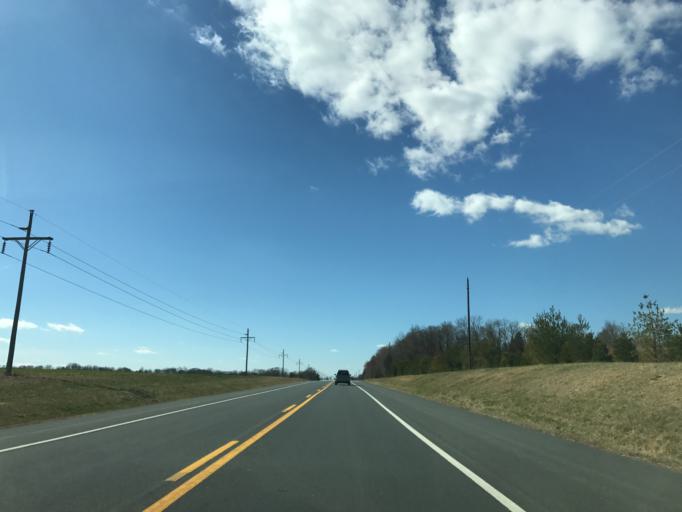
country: US
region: Maryland
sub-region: Queen Anne's County
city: Kingstown
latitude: 39.2561
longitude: -75.9705
